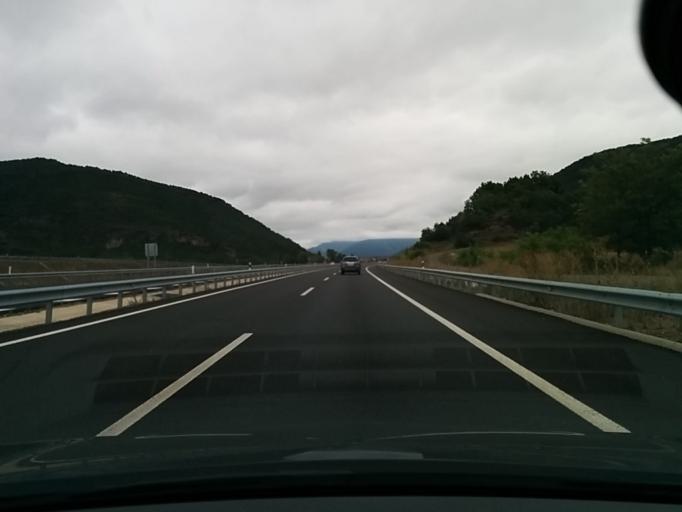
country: ES
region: Aragon
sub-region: Provincia de Huesca
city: Sabinanigo
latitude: 42.4849
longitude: -0.3745
